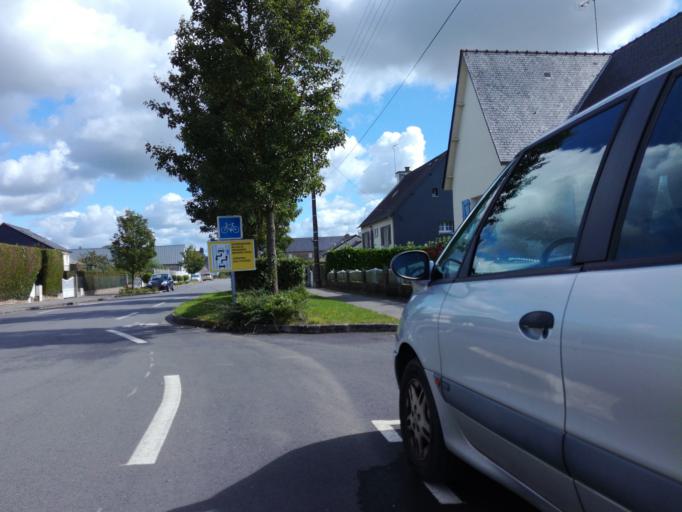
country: FR
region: Brittany
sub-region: Departement d'Ille-et-Vilaine
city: Saint-Aubin-du-Cormier
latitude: 48.2577
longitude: -1.3999
